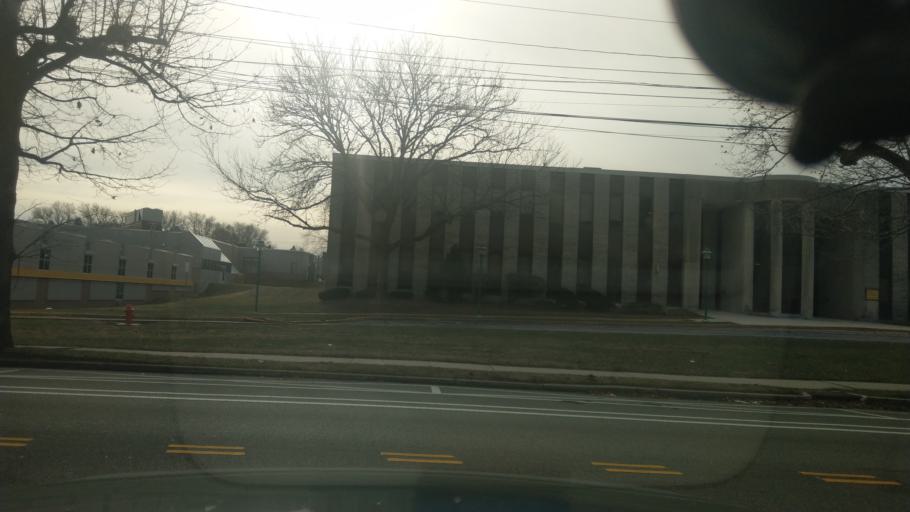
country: US
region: Pennsylvania
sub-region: Montgomery County
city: Wyncote
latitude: 40.0472
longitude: -75.1399
